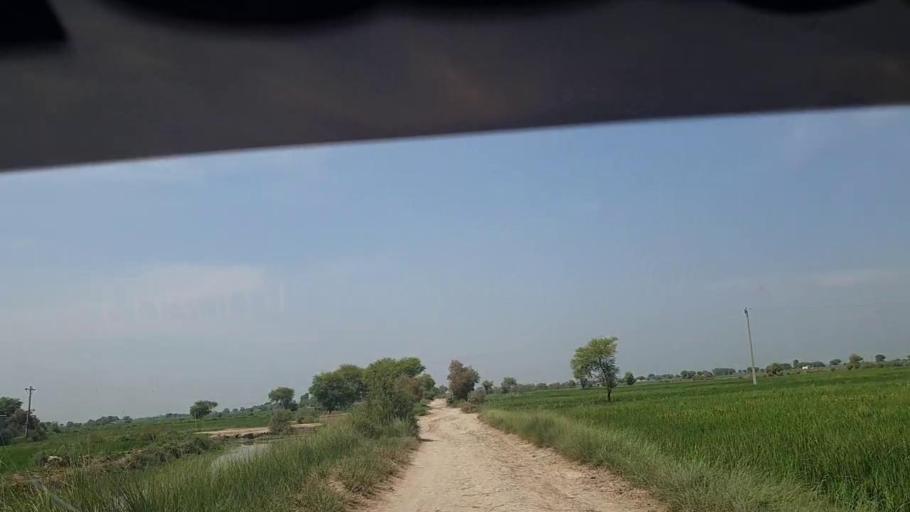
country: PK
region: Sindh
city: Thul
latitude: 28.1887
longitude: 68.7161
